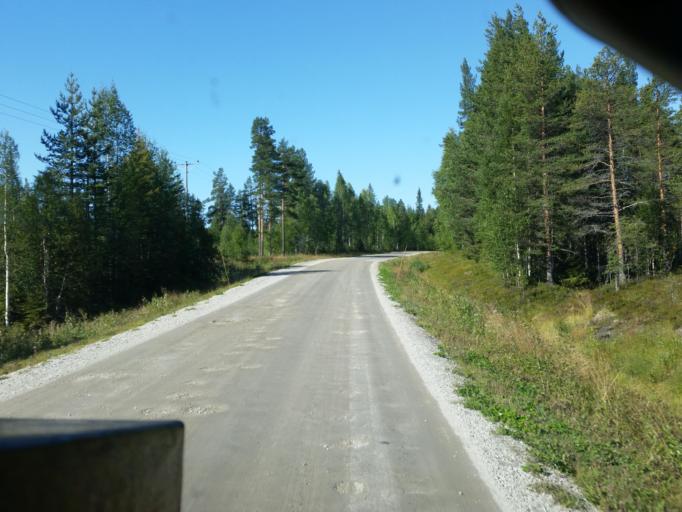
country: SE
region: Vaesterbotten
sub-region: Skelleftea Kommun
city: Backa
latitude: 65.2003
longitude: 20.9889
